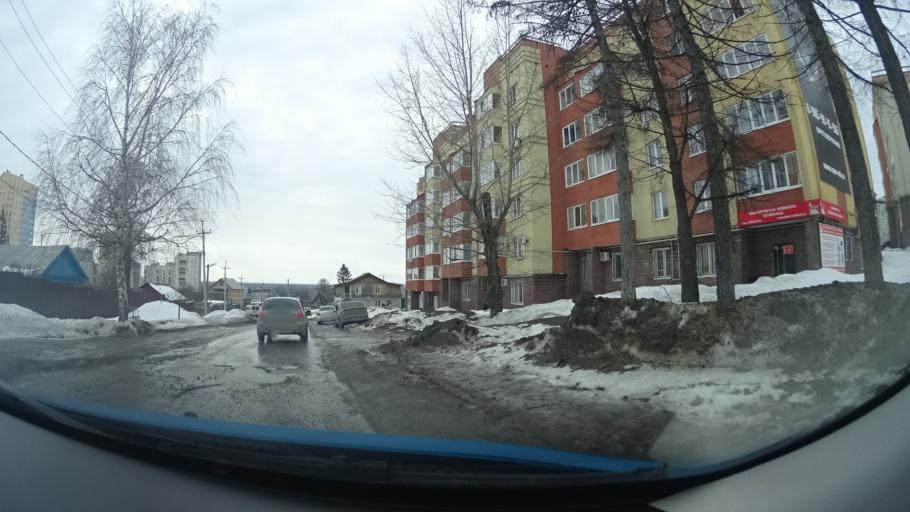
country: RU
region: Bashkortostan
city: Ufa
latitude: 54.6930
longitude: 55.9883
